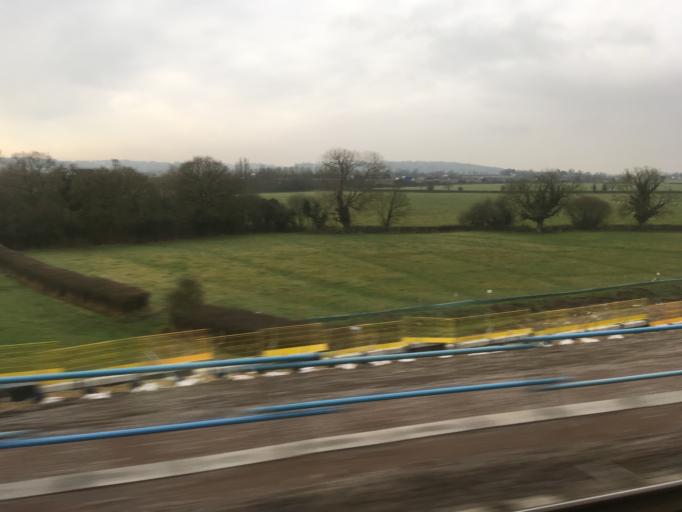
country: GB
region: England
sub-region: Wiltshire
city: Royal Wootton Bassett
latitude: 51.5523
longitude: -1.9361
